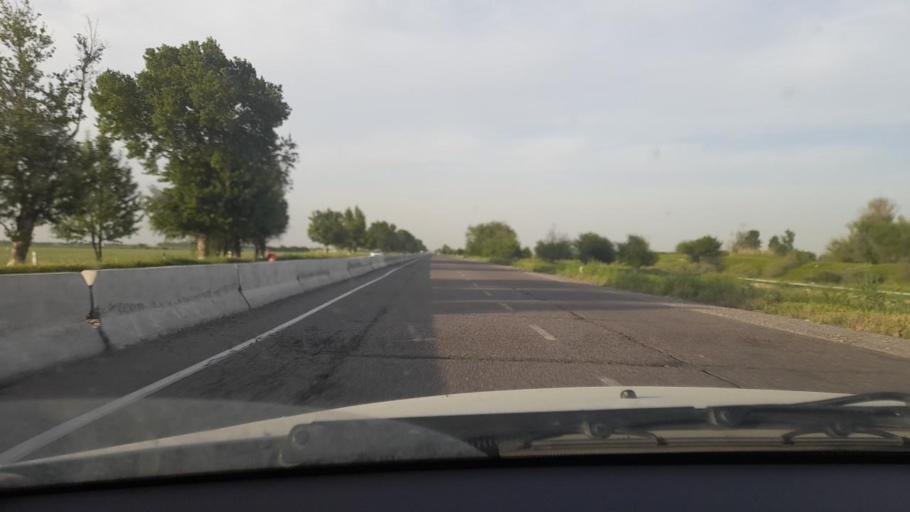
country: KZ
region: Ongtustik Qazaqstan
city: Myrzakent
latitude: 40.5443
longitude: 68.3548
